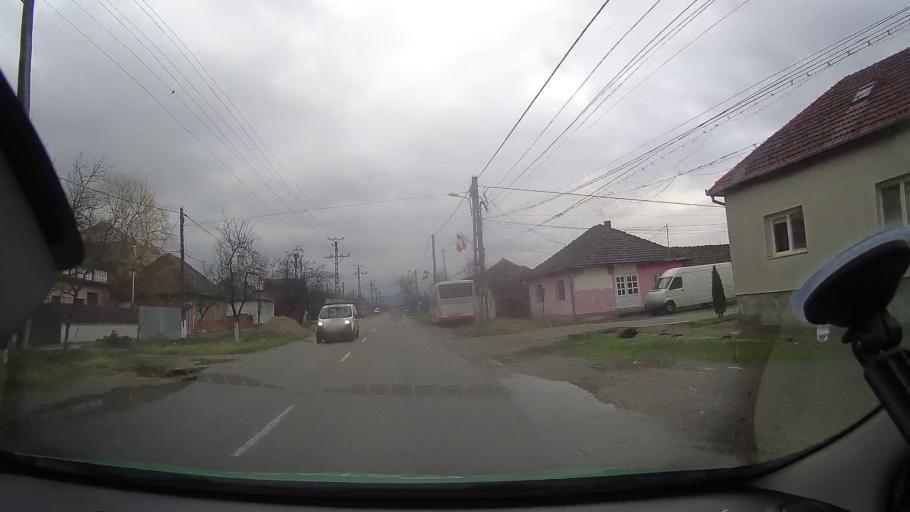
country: RO
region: Arad
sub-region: Comuna Sebis
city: Sebis
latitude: 46.3645
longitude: 22.1308
